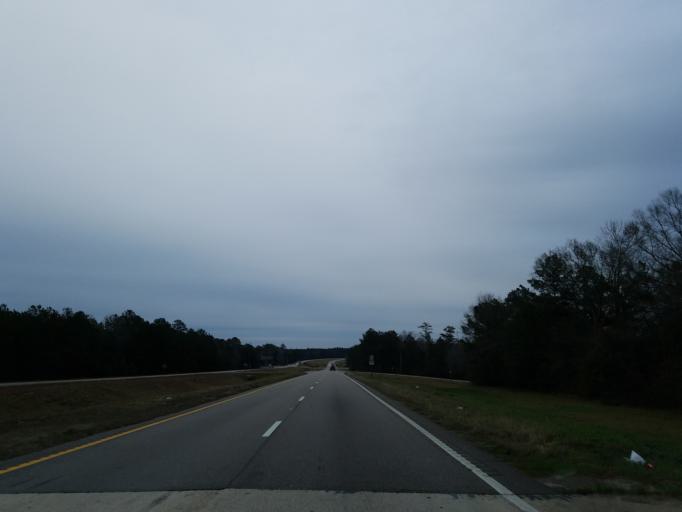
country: US
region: Mississippi
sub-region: Forrest County
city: Hattiesburg
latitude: 31.2449
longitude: -89.2478
